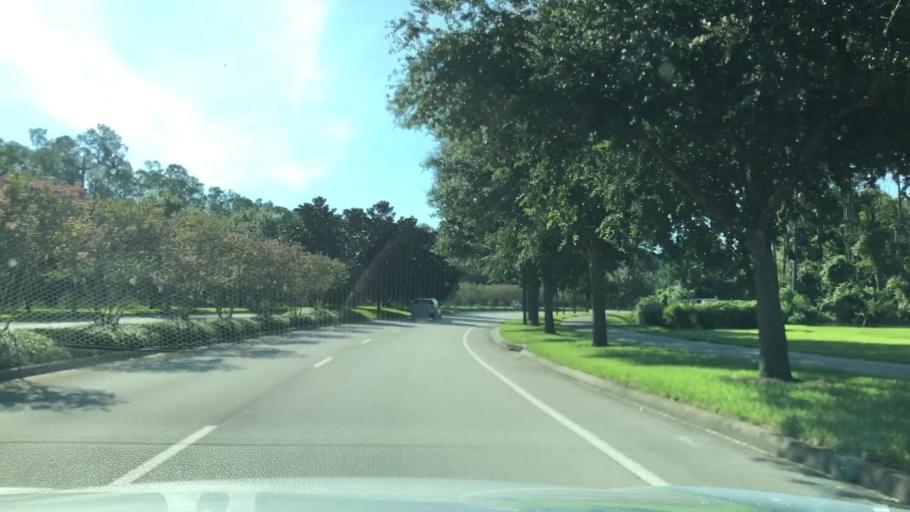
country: US
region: Florida
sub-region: Saint Johns County
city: Palm Valley
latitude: 30.1015
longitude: -81.4119
